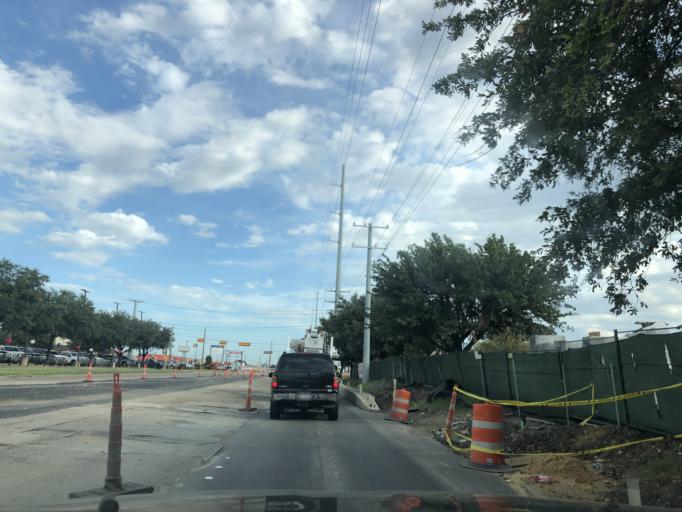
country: US
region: Texas
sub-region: Dallas County
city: Garland
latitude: 32.8749
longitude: -96.6653
